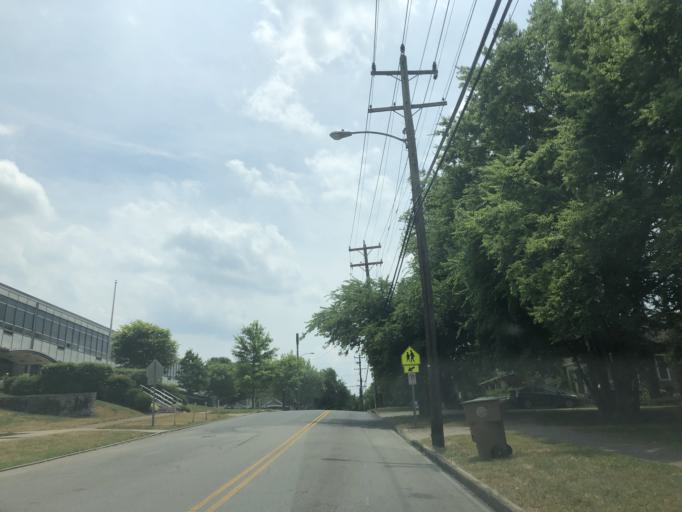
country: US
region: Tennessee
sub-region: Davidson County
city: Nashville
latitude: 36.1328
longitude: -86.8058
